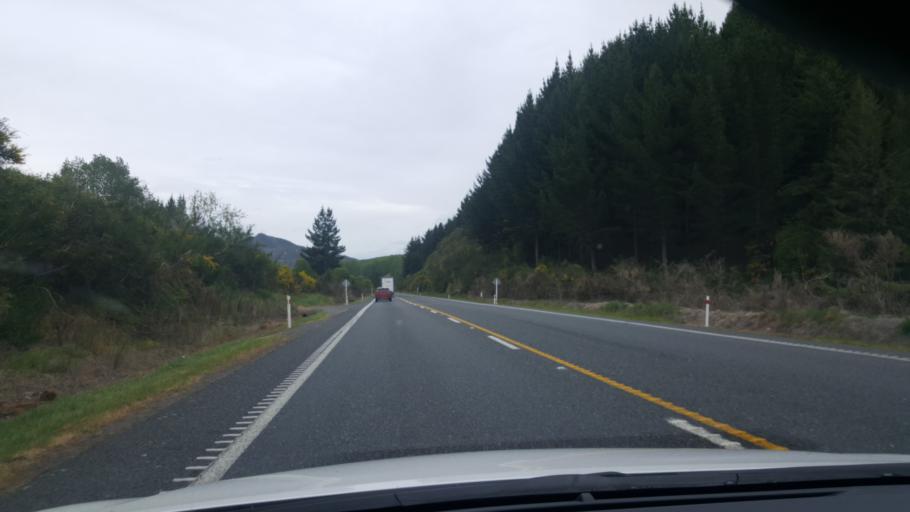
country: NZ
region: Bay of Plenty
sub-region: Rotorua District
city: Rotorua
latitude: -38.2900
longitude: 176.3523
